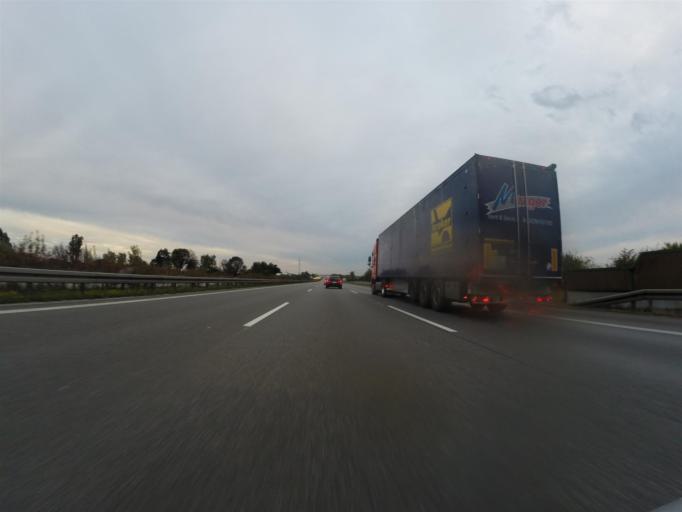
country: DE
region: Thuringia
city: Walpernhain
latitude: 51.0319
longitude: 11.9382
